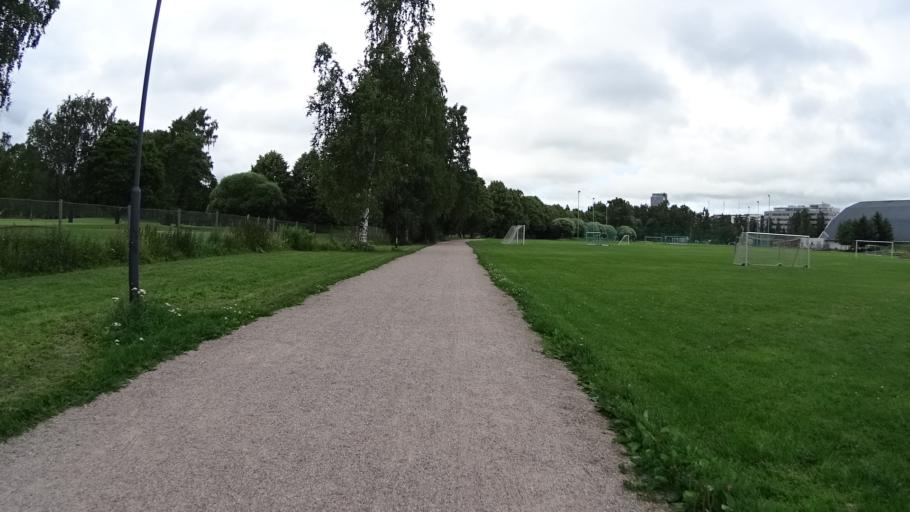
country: FI
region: Uusimaa
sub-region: Helsinki
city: Teekkarikylae
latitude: 60.2125
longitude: 24.8654
